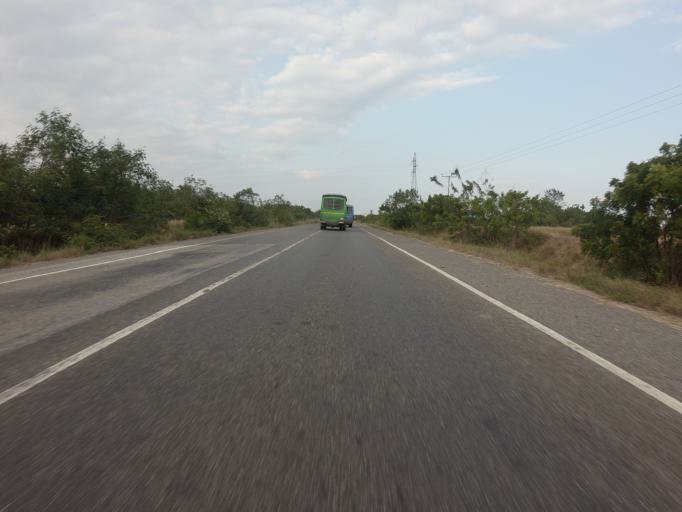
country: GH
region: Volta
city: Anloga
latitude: 6.0901
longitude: 0.5251
